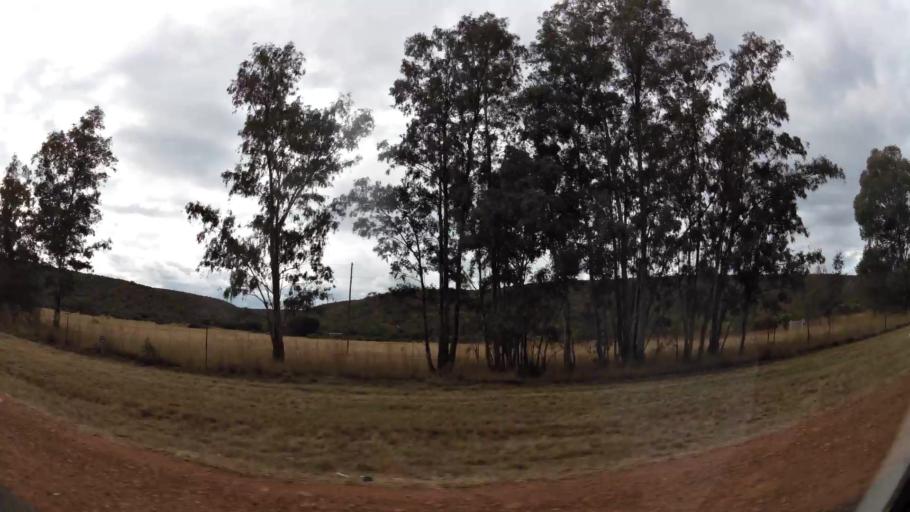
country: ZA
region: Limpopo
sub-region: Waterberg District Municipality
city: Modimolle
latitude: -24.6730
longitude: 28.5034
